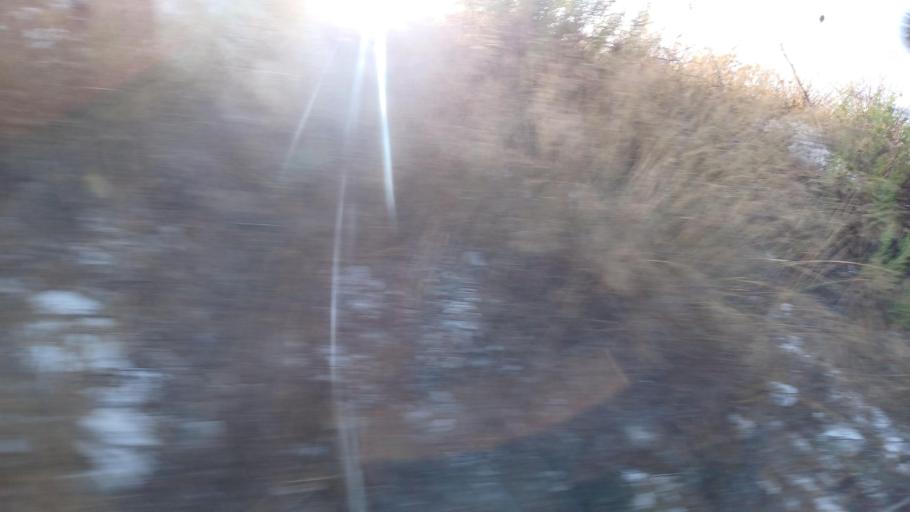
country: CY
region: Pafos
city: Mesogi
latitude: 34.8619
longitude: 32.5131
